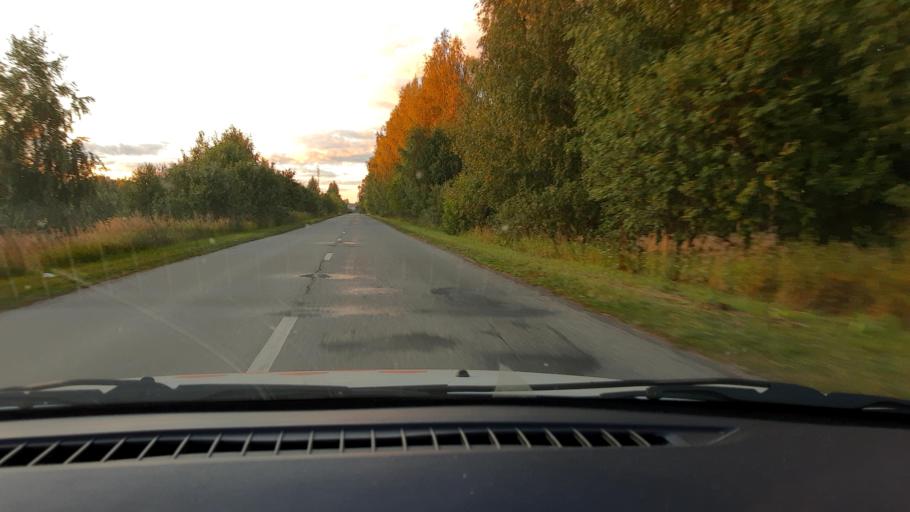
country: RU
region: Nizjnij Novgorod
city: Zavolzh'ye
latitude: 56.7041
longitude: 43.4162
